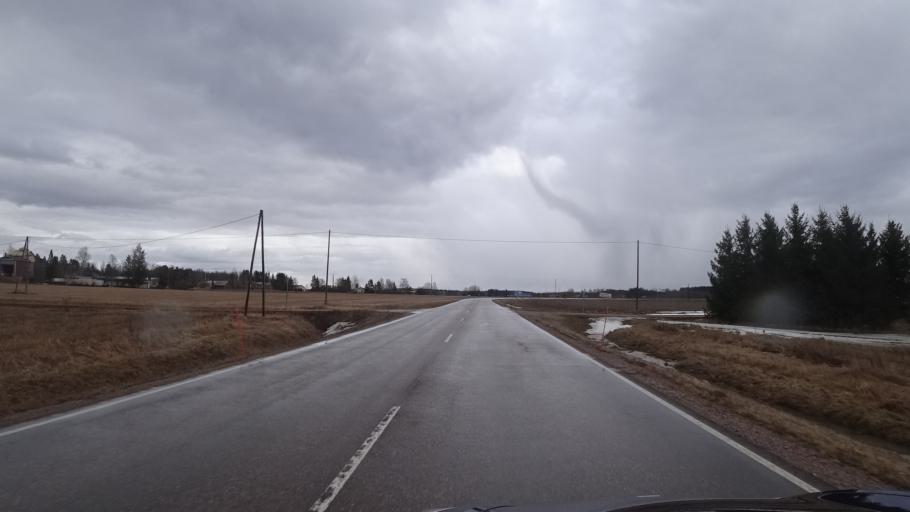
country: FI
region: Uusimaa
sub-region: Loviisa
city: Lapinjaervi
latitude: 60.7039
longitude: 26.2985
